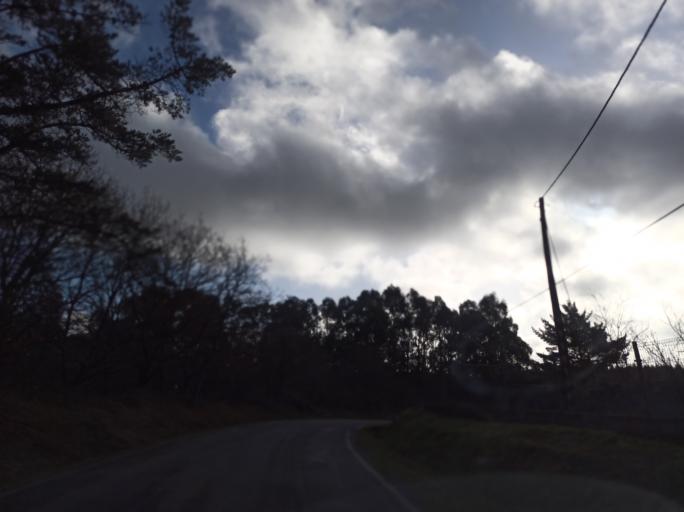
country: ES
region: Galicia
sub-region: Provincia da Coruna
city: Curtis
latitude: 43.0979
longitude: -7.9812
